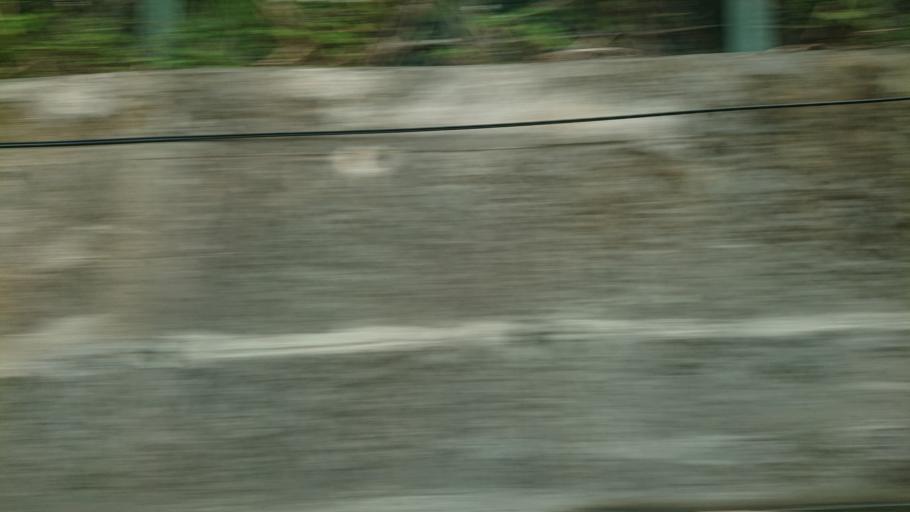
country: TW
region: Taiwan
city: Daxi
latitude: 24.8665
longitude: 121.4203
